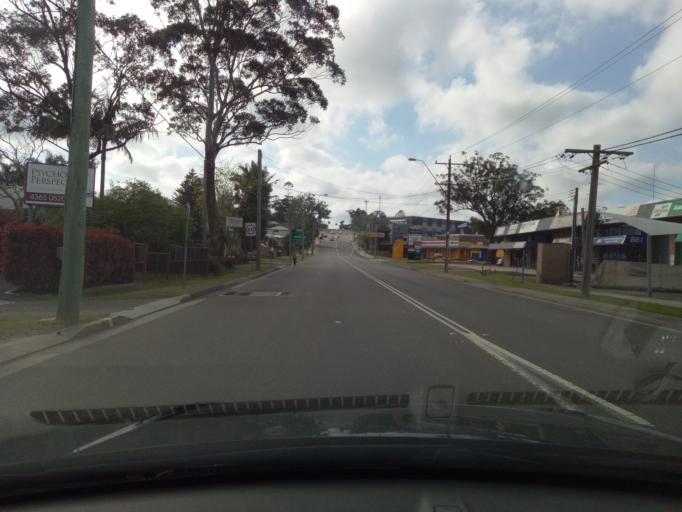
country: AU
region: New South Wales
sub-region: Gosford Shire
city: Erina
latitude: -33.4334
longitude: 151.3867
